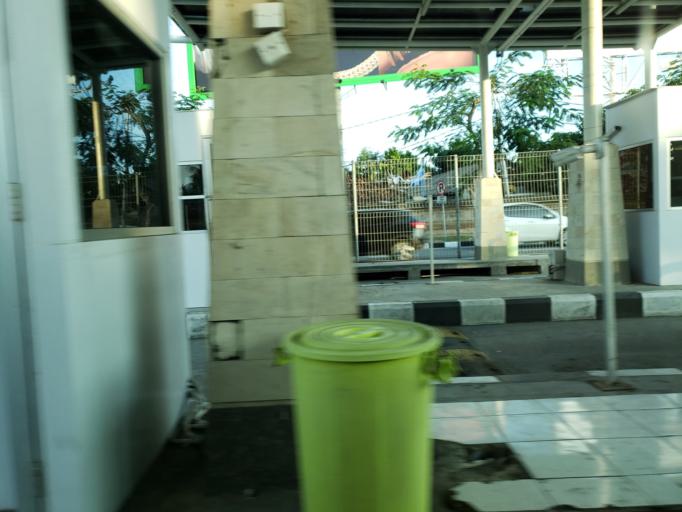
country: ID
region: Bali
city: Kelanabian
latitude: -8.7416
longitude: 115.1681
